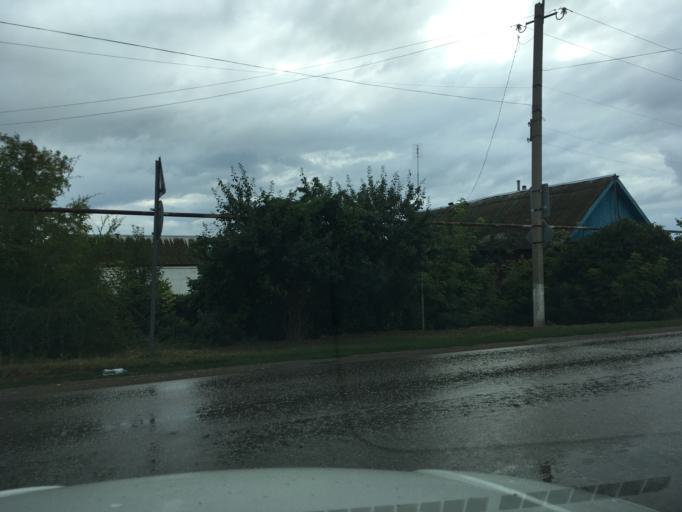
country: RU
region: Samara
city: Bezenchuk
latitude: 52.9799
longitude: 49.4386
